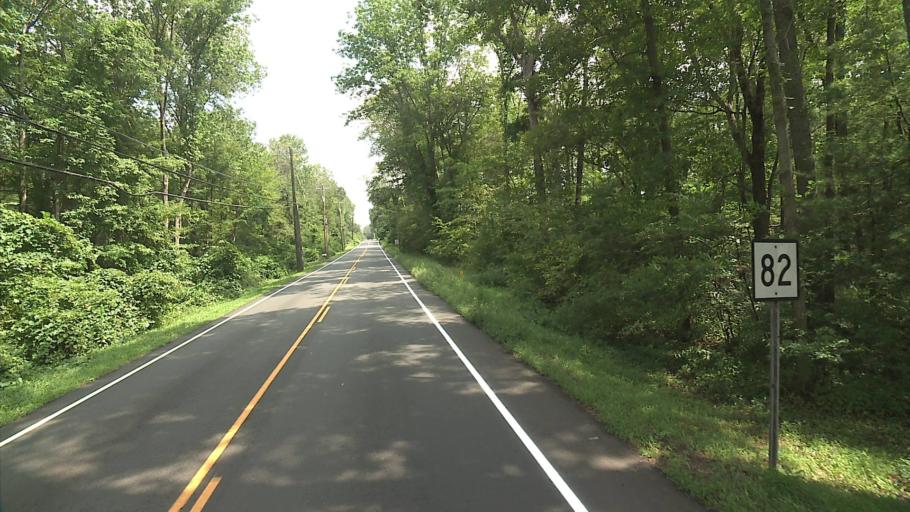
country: US
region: Connecticut
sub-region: New London County
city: Montville Center
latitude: 41.4806
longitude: -72.2597
